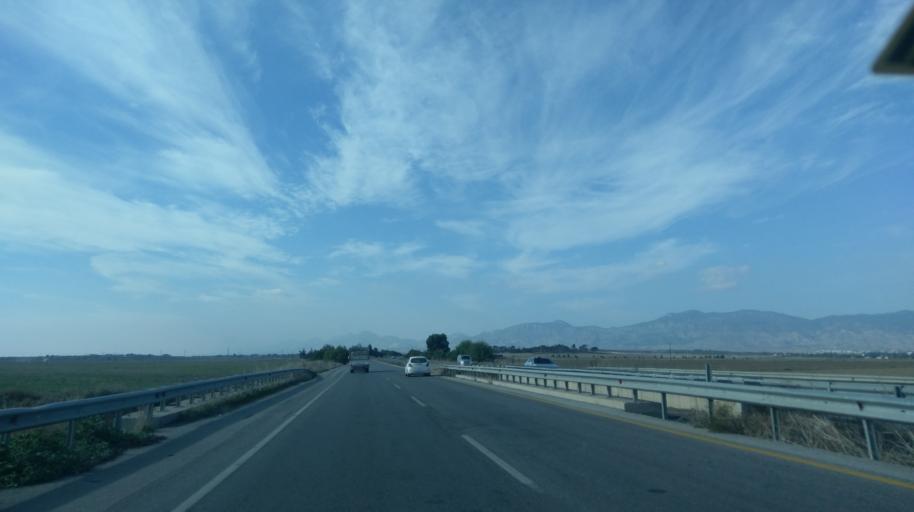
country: CY
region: Ammochostos
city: Lefkonoiko
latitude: 35.1907
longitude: 33.6266
